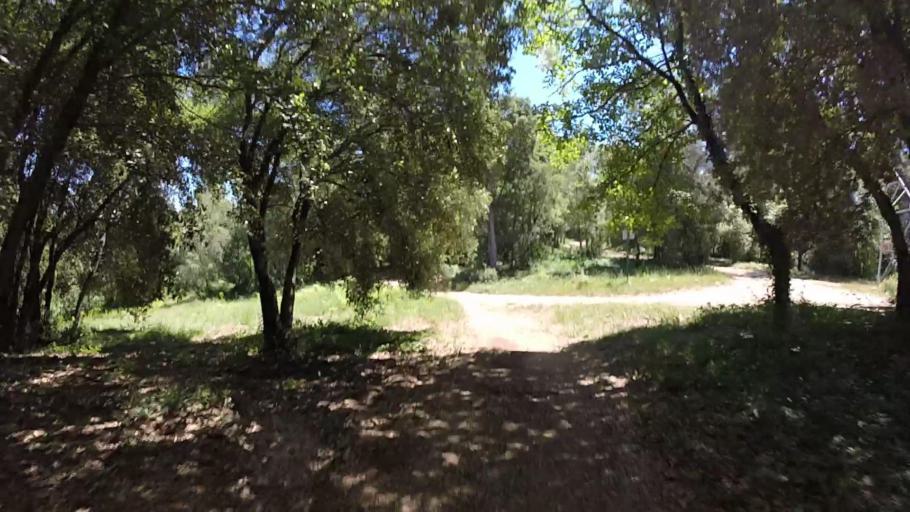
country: FR
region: Provence-Alpes-Cote d'Azur
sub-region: Departement des Alpes-Maritimes
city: Valbonne
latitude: 43.6237
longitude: 7.0248
